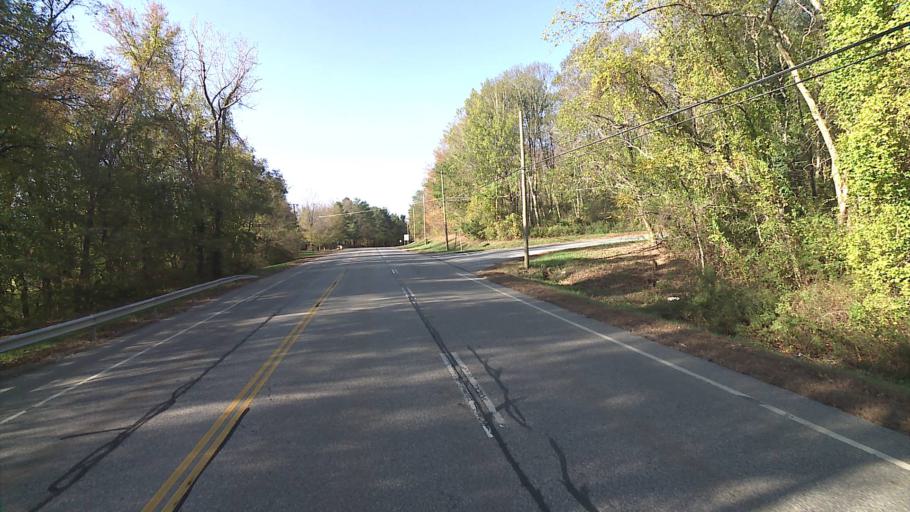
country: US
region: Connecticut
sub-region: Windham County
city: Windham
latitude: 41.7686
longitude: -72.0495
